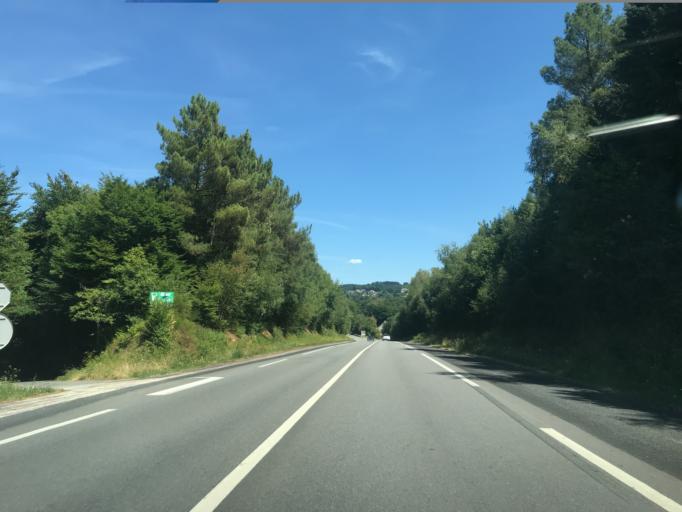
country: FR
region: Limousin
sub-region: Departement de la Correze
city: Naves
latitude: 45.3072
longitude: 1.8211
